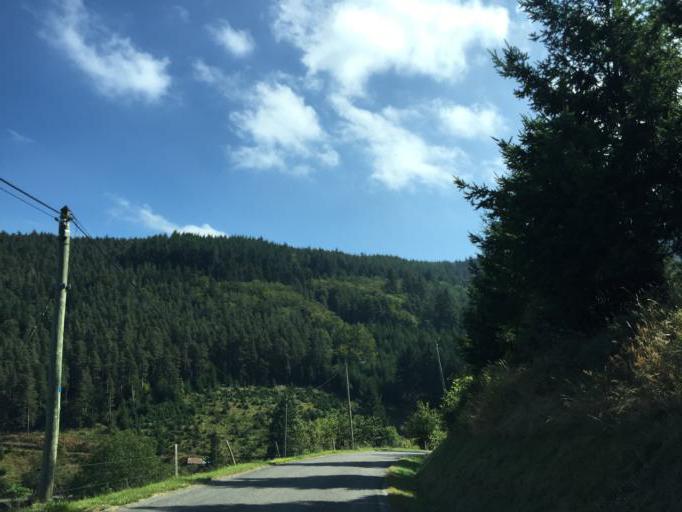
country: FR
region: Rhone-Alpes
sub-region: Departement de la Loire
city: Saint-Paul-en-Jarez
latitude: 45.4201
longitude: 4.5615
